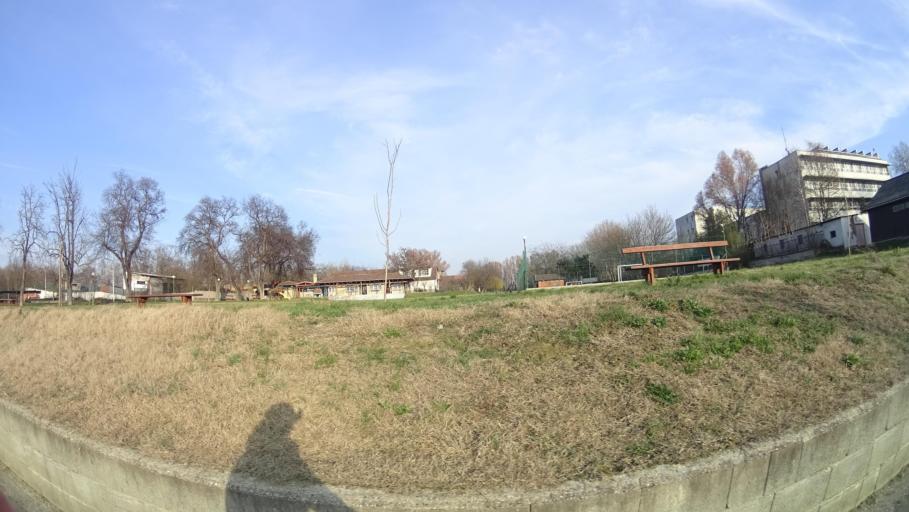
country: HU
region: Pest
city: Szodliget
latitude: 47.7311
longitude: 19.1342
